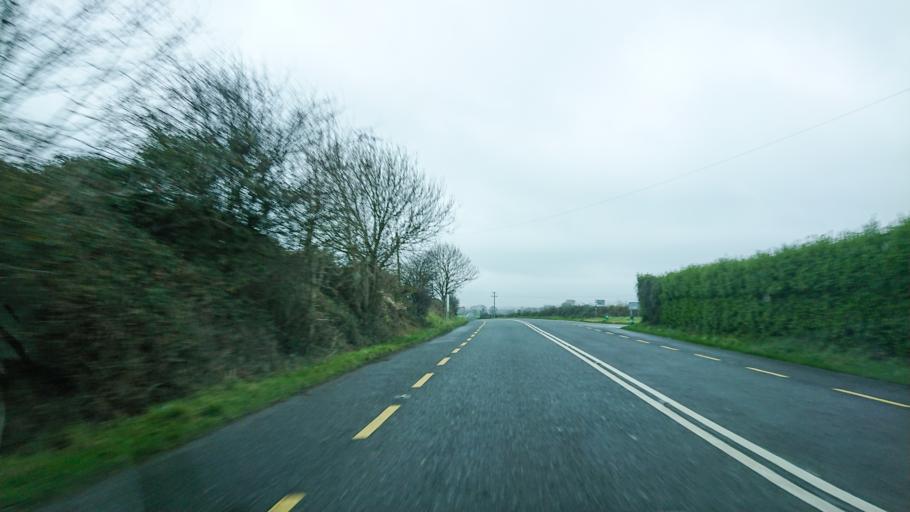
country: IE
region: Leinster
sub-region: Kilkenny
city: Mooncoin
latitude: 52.2889
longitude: -7.2275
